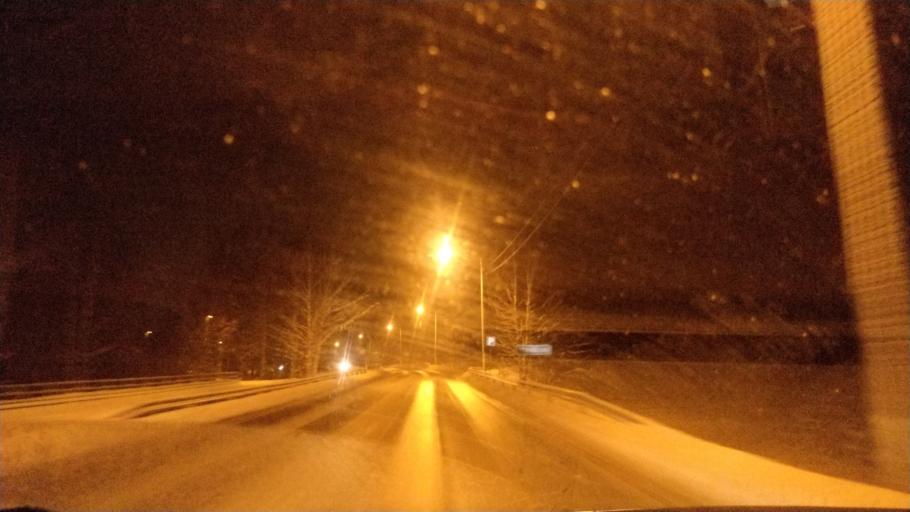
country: FI
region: Lapland
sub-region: Rovaniemi
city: Rovaniemi
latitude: 66.3930
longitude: 25.3808
